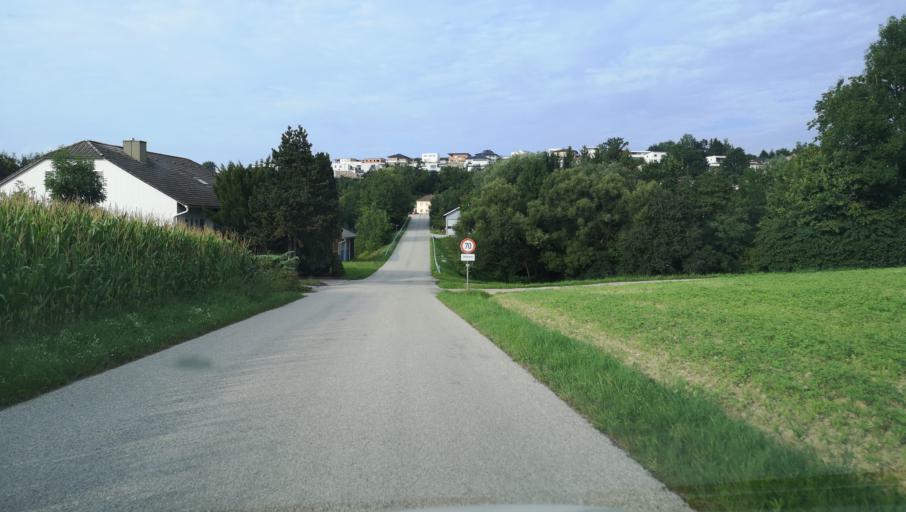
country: AT
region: Lower Austria
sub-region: Politischer Bezirk Amstetten
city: Zeillern
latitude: 48.1731
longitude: 14.8278
